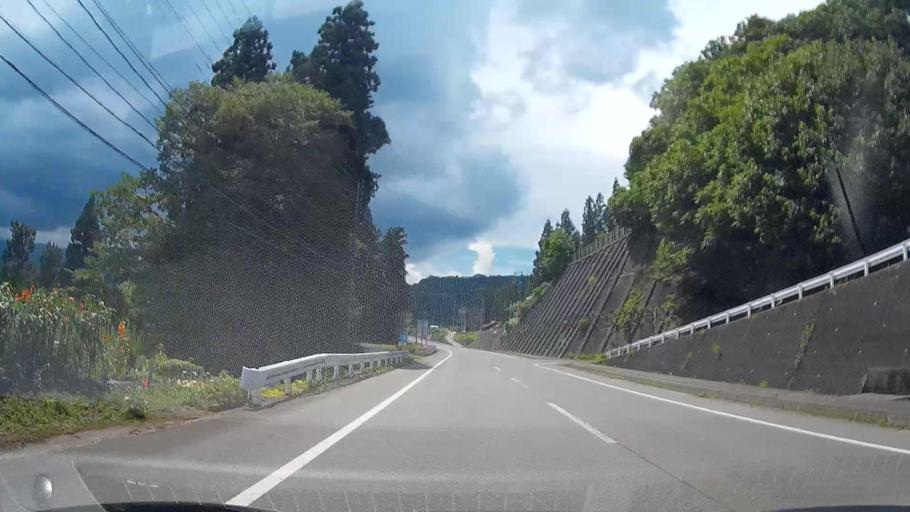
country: JP
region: Niigata
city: Tokamachi
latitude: 36.9911
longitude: 138.5717
